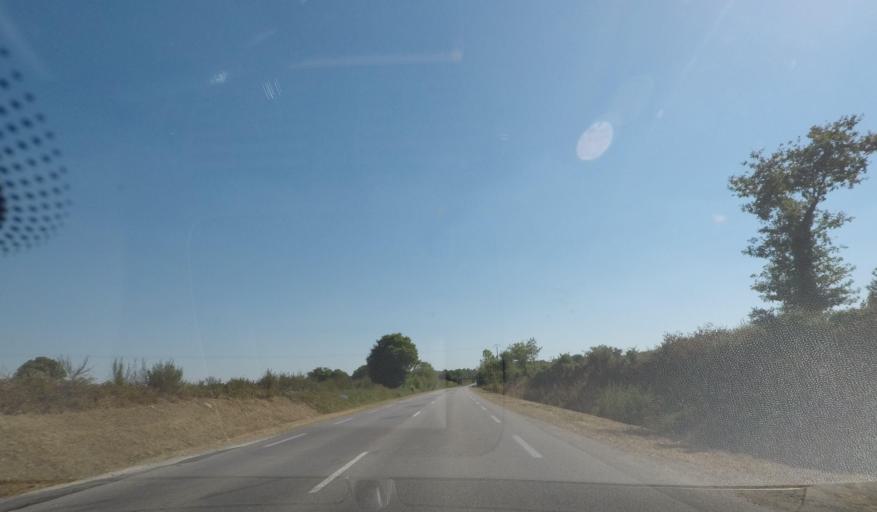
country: FR
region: Brittany
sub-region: Departement du Morbihan
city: Questembert
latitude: 47.6628
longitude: -2.4277
